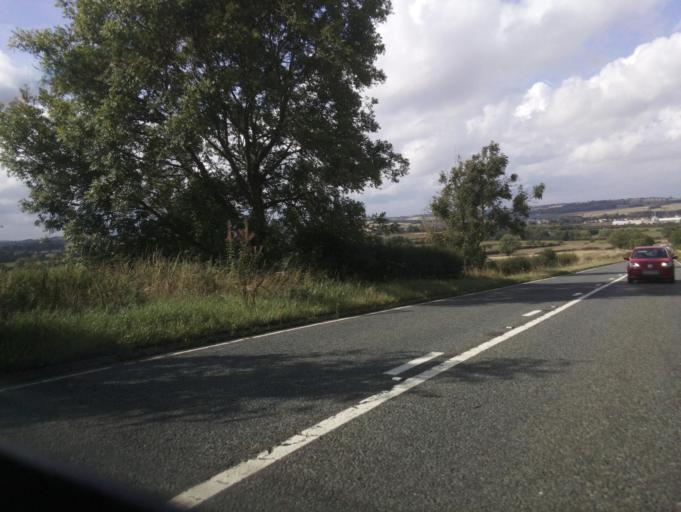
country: GB
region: England
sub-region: County Durham
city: Bishop Auckland
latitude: 54.6182
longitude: -1.7051
